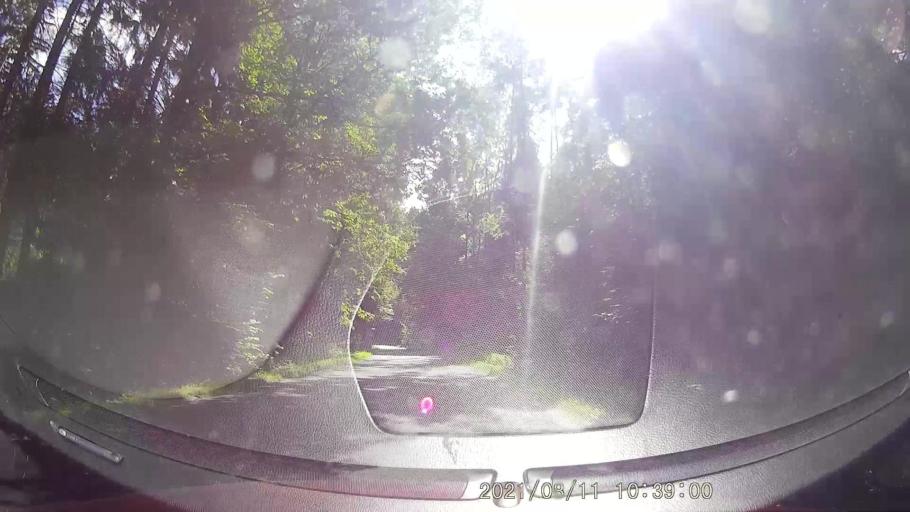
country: PL
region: Lower Silesian Voivodeship
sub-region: Powiat klodzki
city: Polanica-Zdroj
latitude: 50.3969
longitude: 16.4875
